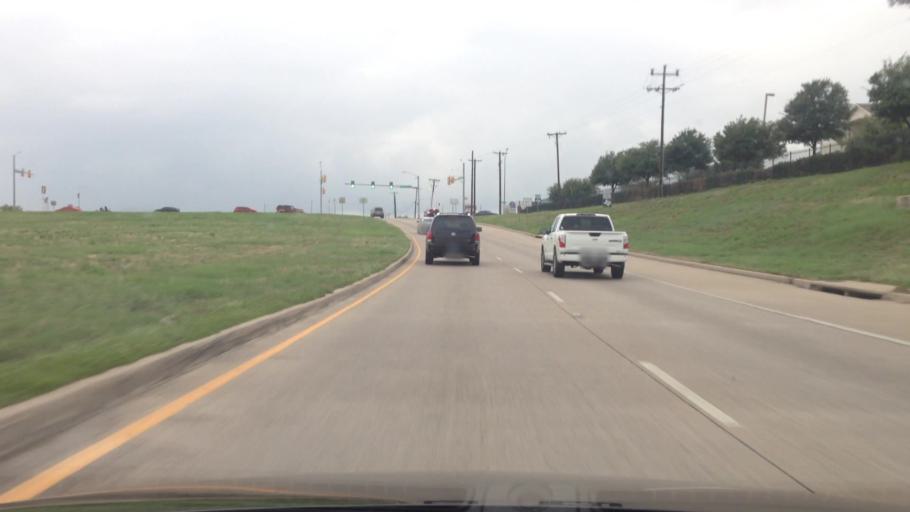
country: US
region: Texas
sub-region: Tarrant County
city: Crowley
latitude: 32.5779
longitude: -97.3269
